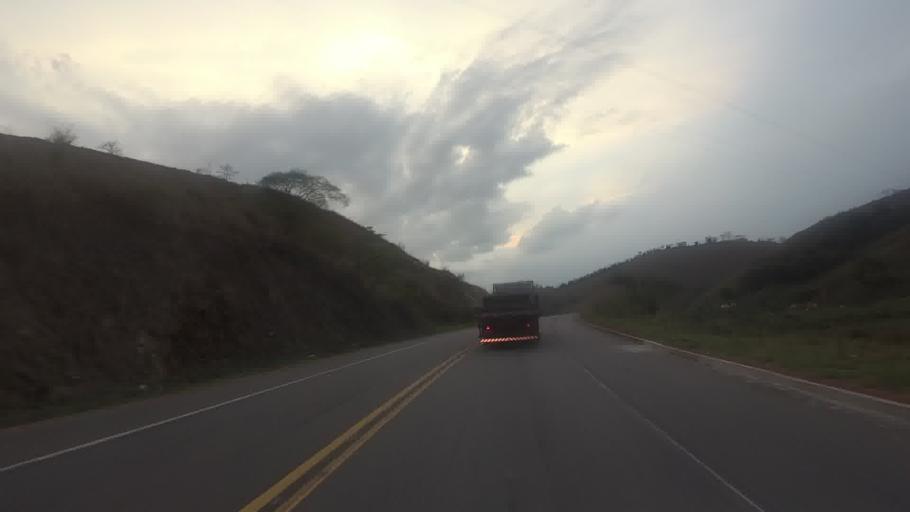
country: BR
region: Minas Gerais
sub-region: Alem Paraiba
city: Alem Paraiba
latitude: -21.8553
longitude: -42.6500
